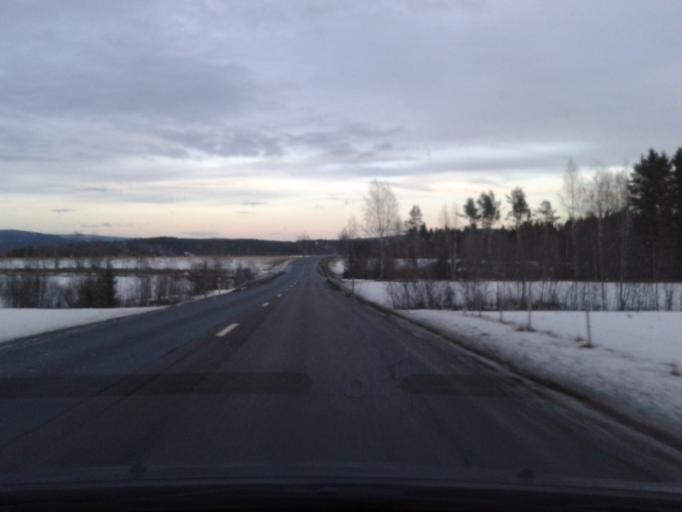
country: SE
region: Vaesternorrland
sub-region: Solleftea Kommun
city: Solleftea
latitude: 63.1485
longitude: 17.3654
